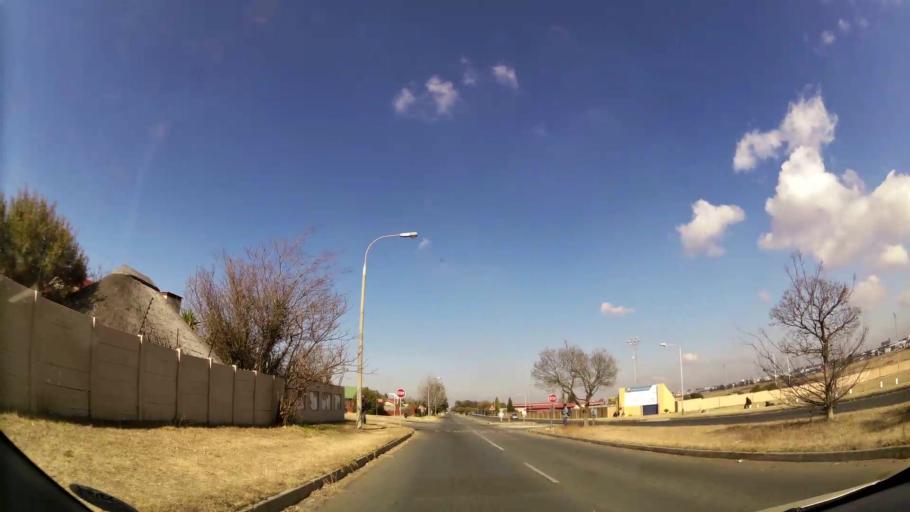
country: ZA
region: Gauteng
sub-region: City of Johannesburg Metropolitan Municipality
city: Roodepoort
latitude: -26.1469
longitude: 27.8242
